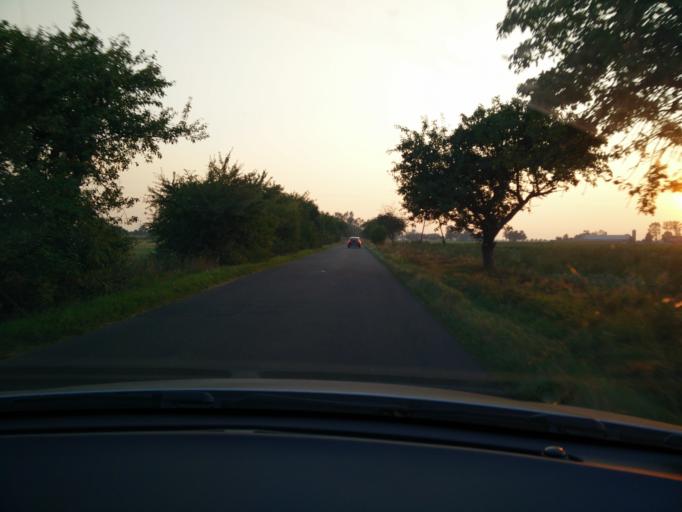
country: PL
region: Greater Poland Voivodeship
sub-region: Powiat wrzesinski
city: Miloslaw
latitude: 52.2444
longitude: 17.5286
